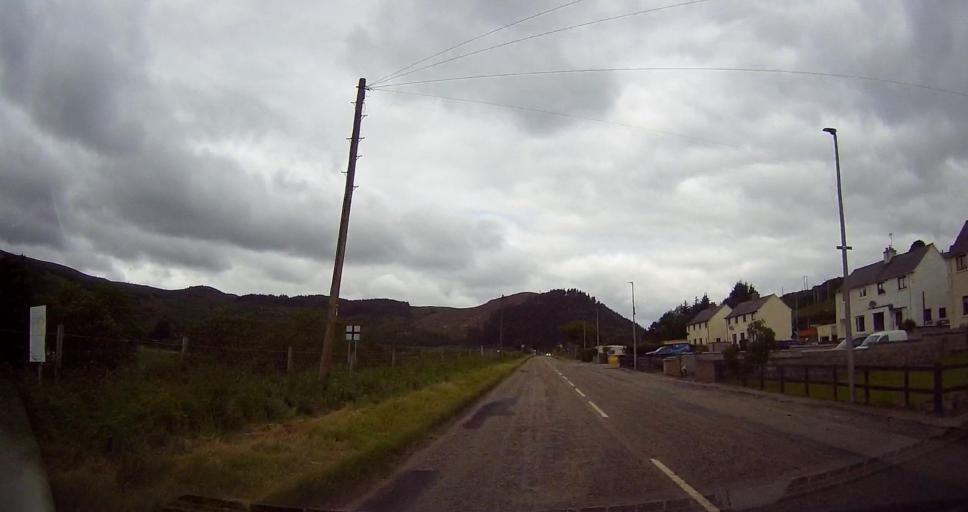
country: GB
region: Scotland
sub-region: Highland
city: Dornoch
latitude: 57.9909
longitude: -4.1632
